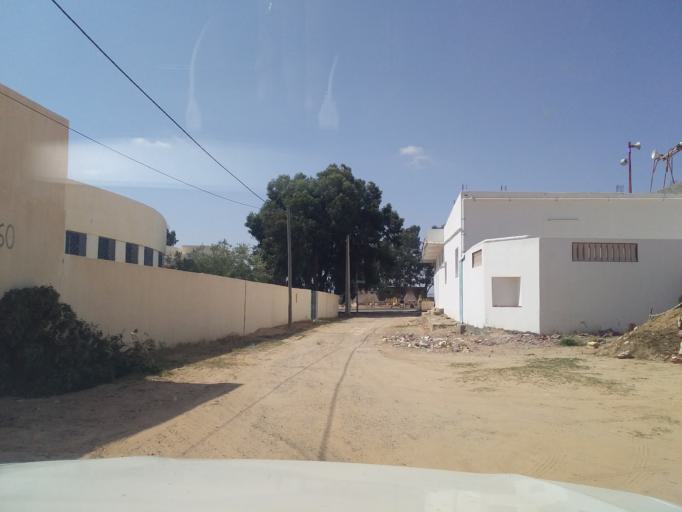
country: TN
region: Madanin
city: Medenine
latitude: 33.6040
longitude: 10.3054
